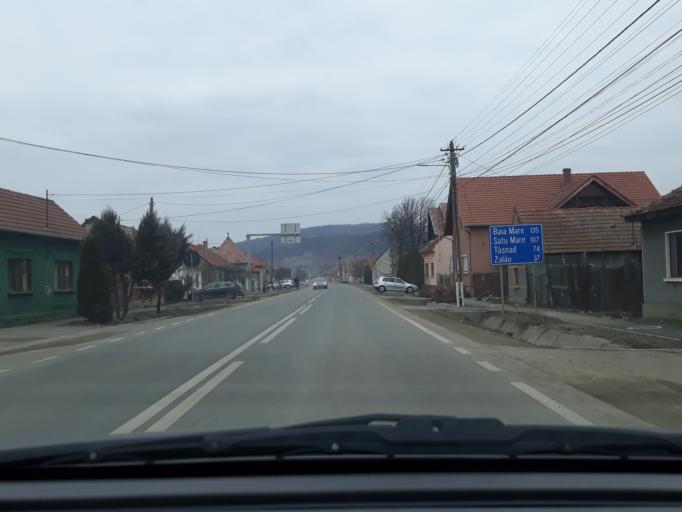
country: RO
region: Salaj
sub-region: Comuna Nusfalau
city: Nusfalau
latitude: 47.2006
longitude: 22.7114
